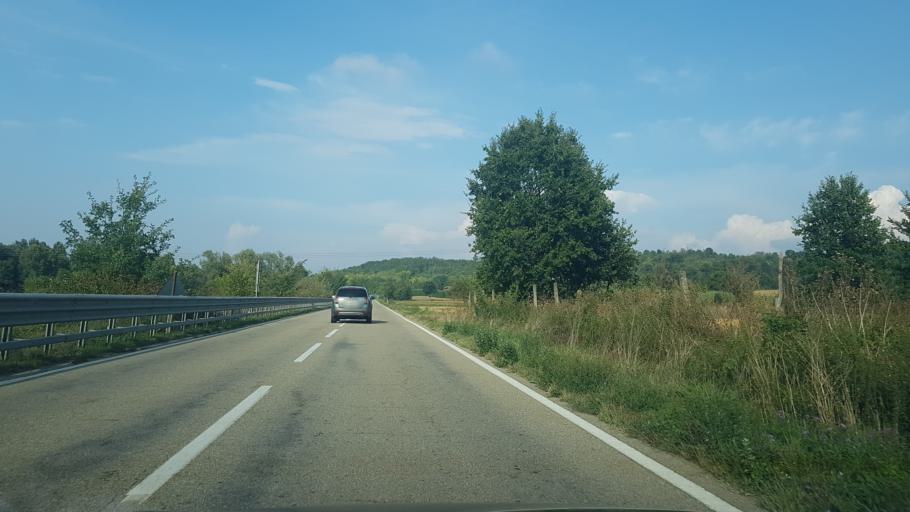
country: IT
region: Piedmont
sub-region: Provincia di Asti
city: Bruno
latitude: 44.8070
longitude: 8.4521
